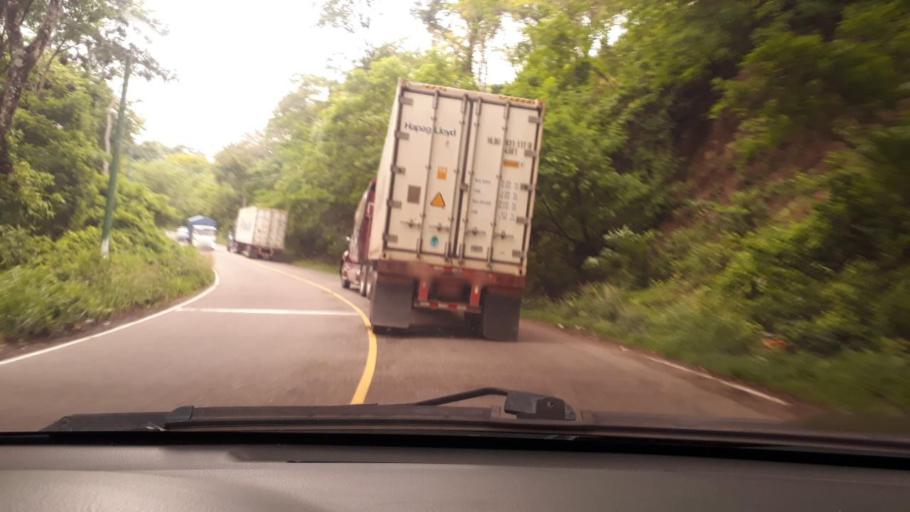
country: GT
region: Chiquimula
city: Quezaltepeque
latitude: 14.6057
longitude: -89.4500
